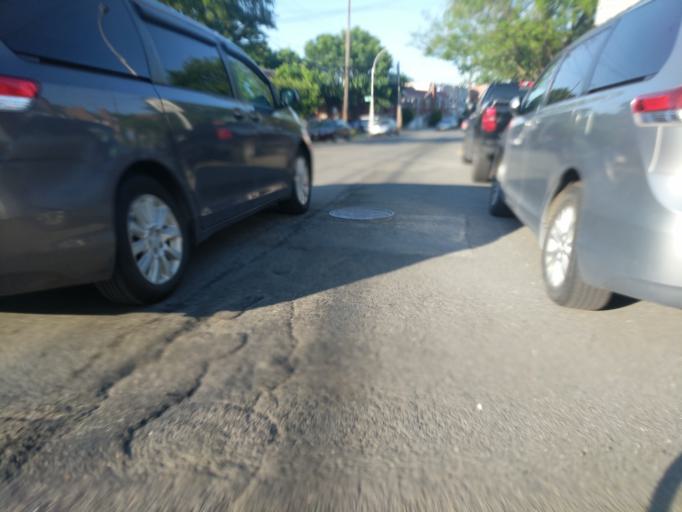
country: US
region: New York
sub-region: Queens County
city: Long Island City
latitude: 40.7349
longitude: -73.8997
